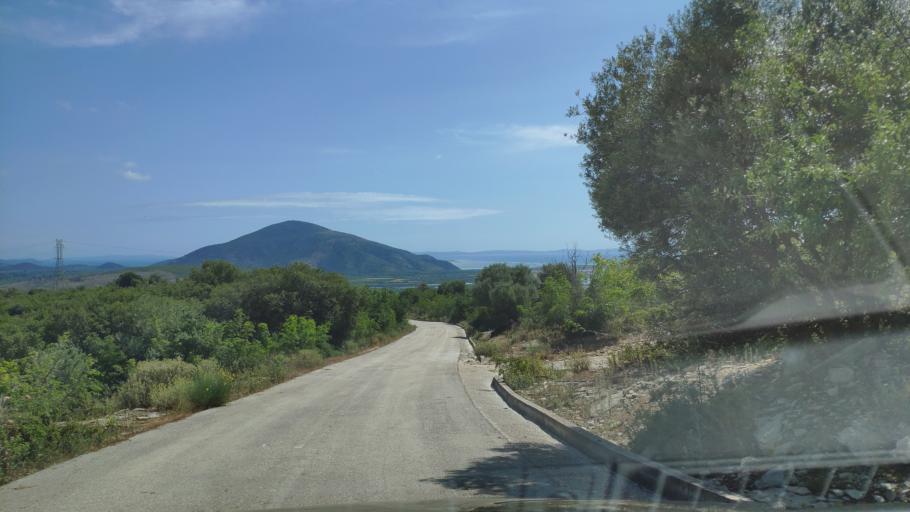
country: AL
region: Vlore
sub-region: Rrethi i Sarandes
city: Konispol
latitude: 39.6302
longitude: 20.2110
